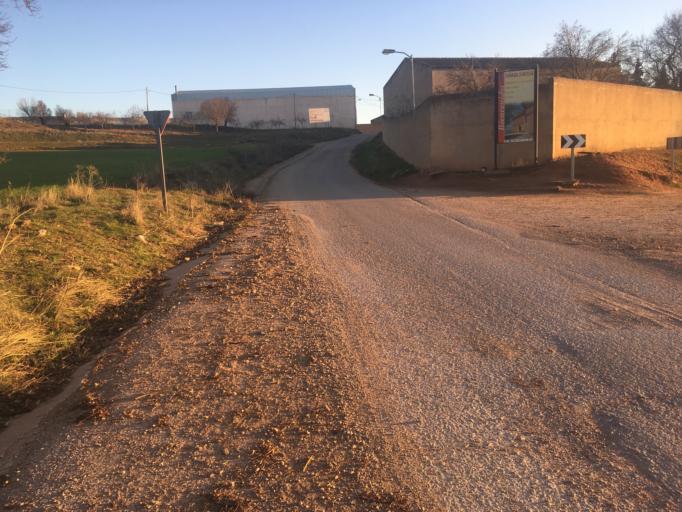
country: ES
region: Castille-La Mancha
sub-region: Provincia de Cuenca
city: Atalaya del Canavate
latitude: 39.5522
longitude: -2.2524
